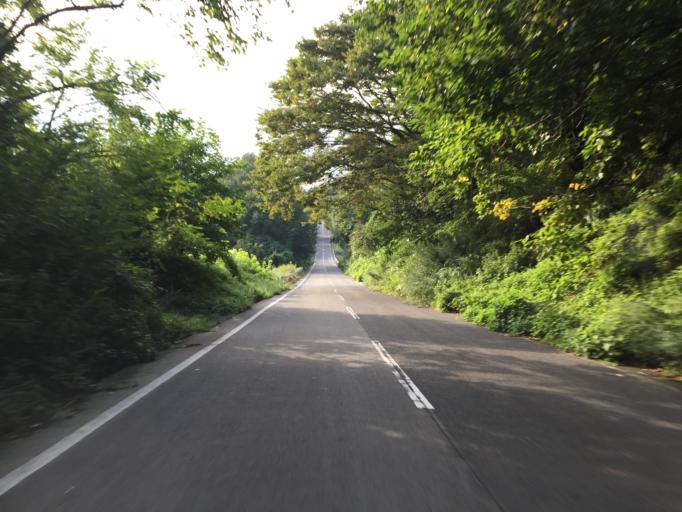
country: JP
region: Fukushima
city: Fukushima-shi
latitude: 37.6548
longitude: 140.5579
